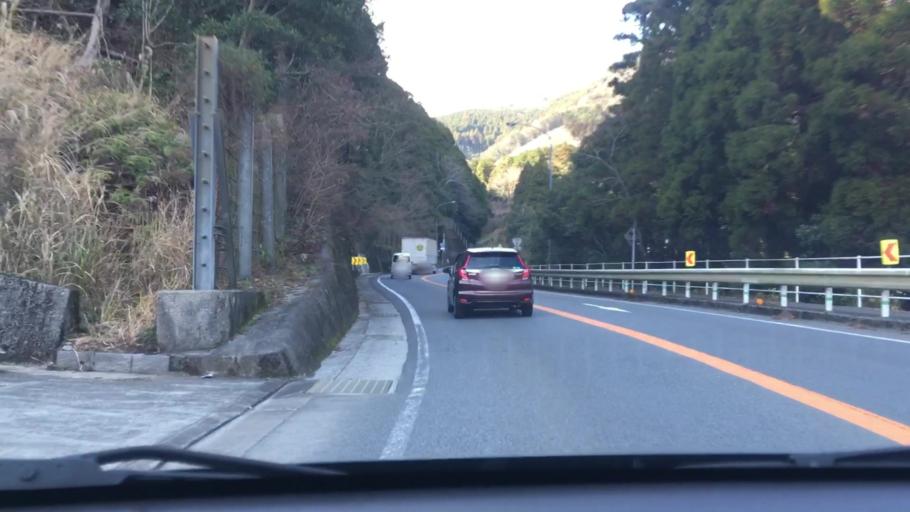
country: JP
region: Oita
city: Tsukumiura
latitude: 32.9989
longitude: 131.8149
